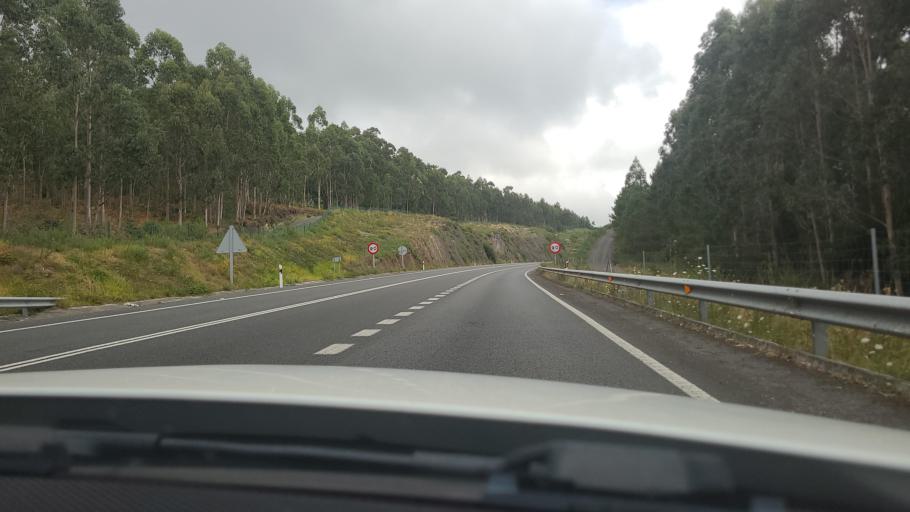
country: ES
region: Galicia
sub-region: Provincia da Coruna
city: Corcubion
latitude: 42.9454
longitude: -9.2238
